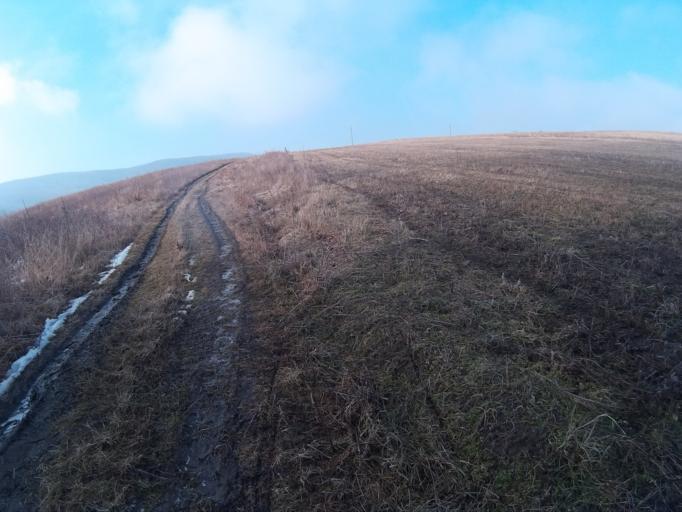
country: HU
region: Nograd
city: Tar
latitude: 47.9980
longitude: 19.6985
